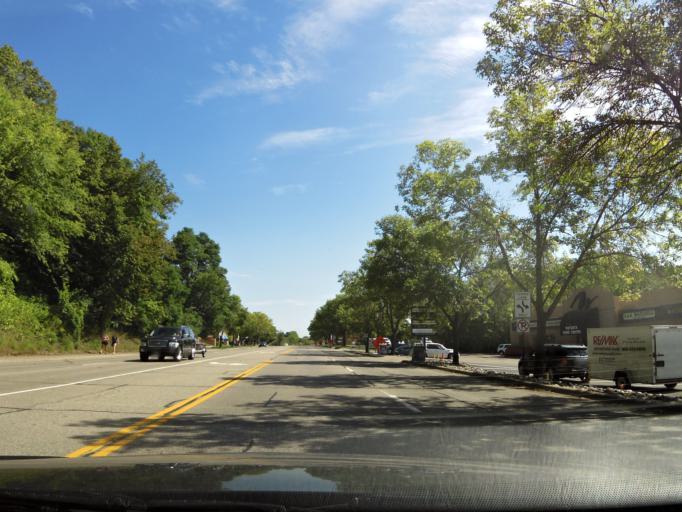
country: US
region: Minnesota
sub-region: Hennepin County
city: Wayzata
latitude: 44.9711
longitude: -93.4984
